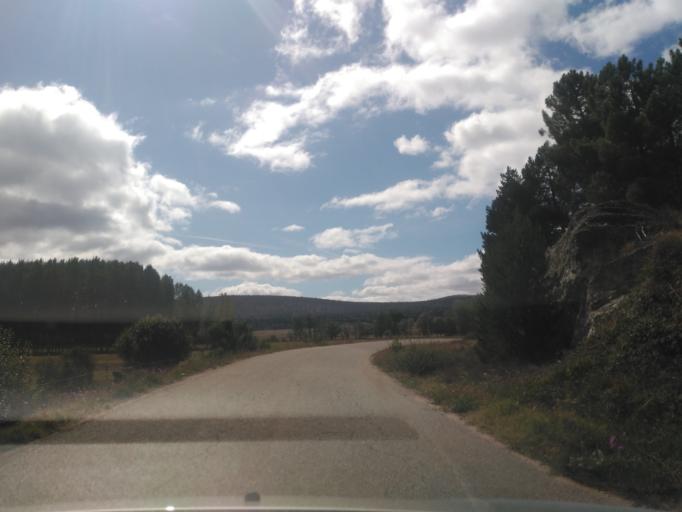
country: ES
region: Castille and Leon
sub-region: Provincia de Burgos
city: Hontoria del Pinar
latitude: 41.8574
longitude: -3.1971
